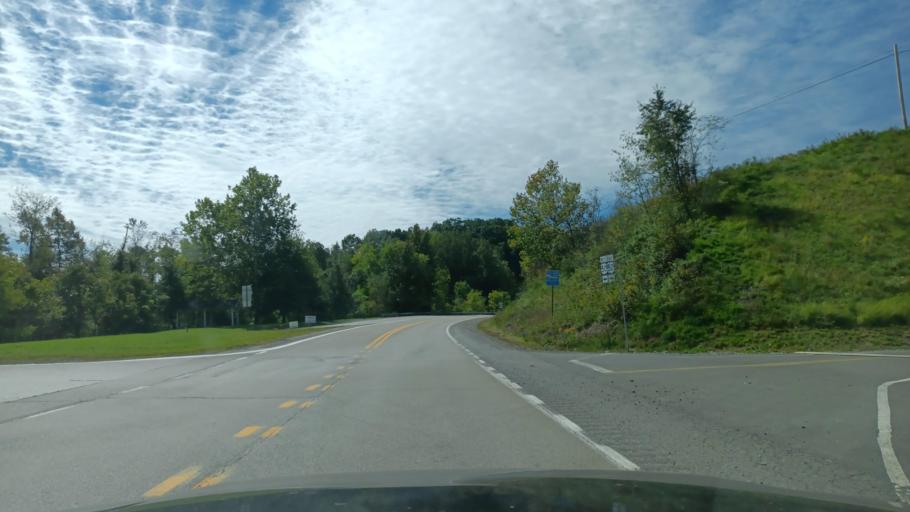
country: US
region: West Virginia
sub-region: Harrison County
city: Bridgeport
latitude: 39.2880
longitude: -80.2287
